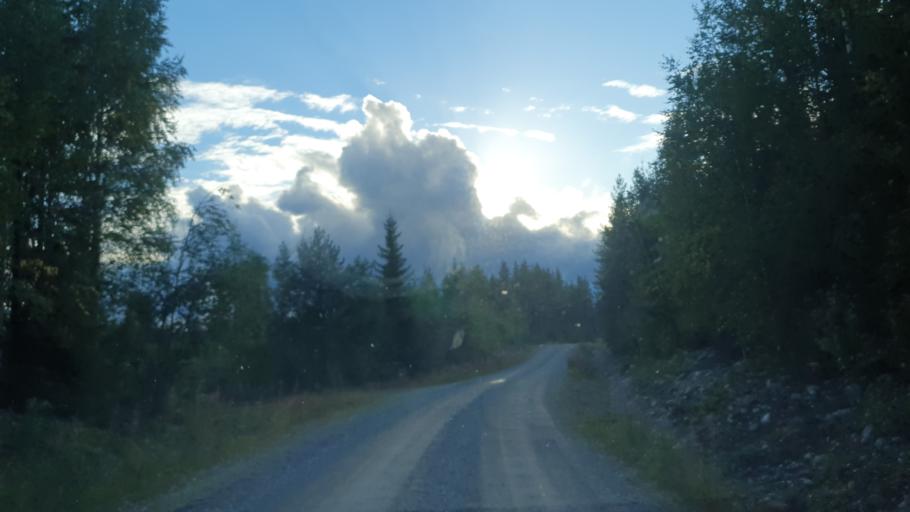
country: FI
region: Kainuu
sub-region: Kehys-Kainuu
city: Kuhmo
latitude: 64.3363
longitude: 29.9521
